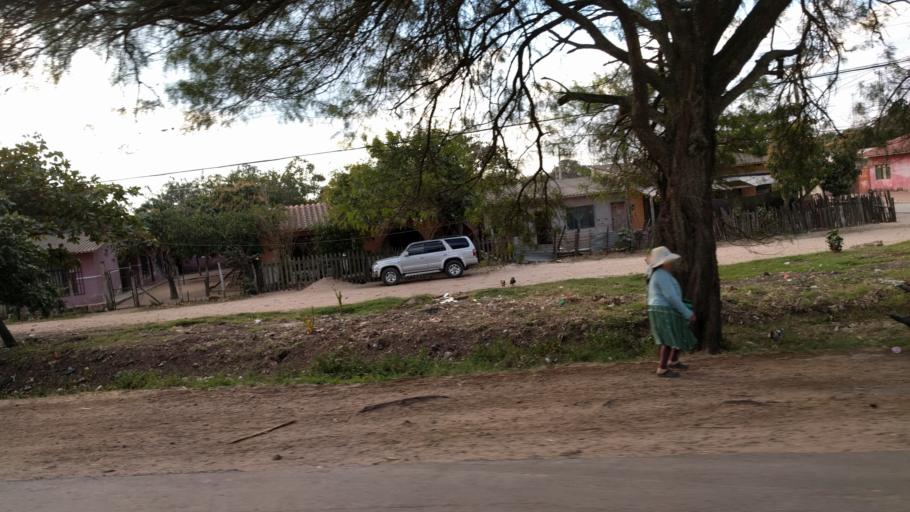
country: BO
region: Santa Cruz
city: Montero
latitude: -17.3185
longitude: -63.2712
